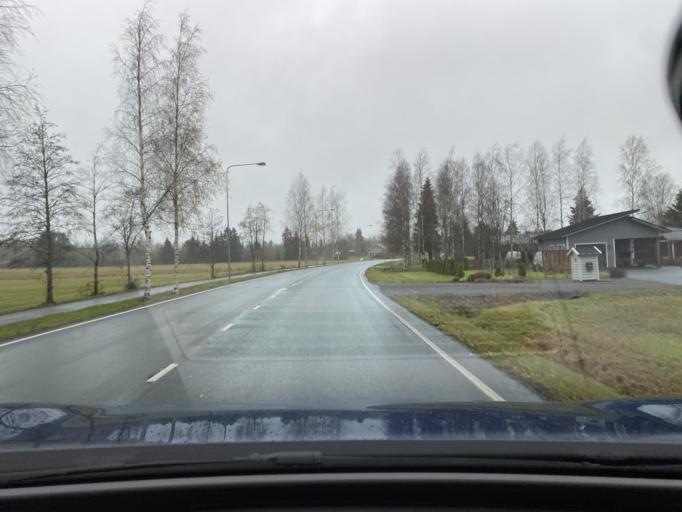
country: FI
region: Varsinais-Suomi
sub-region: Loimaa
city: Alastaro
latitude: 60.9436
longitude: 22.8667
